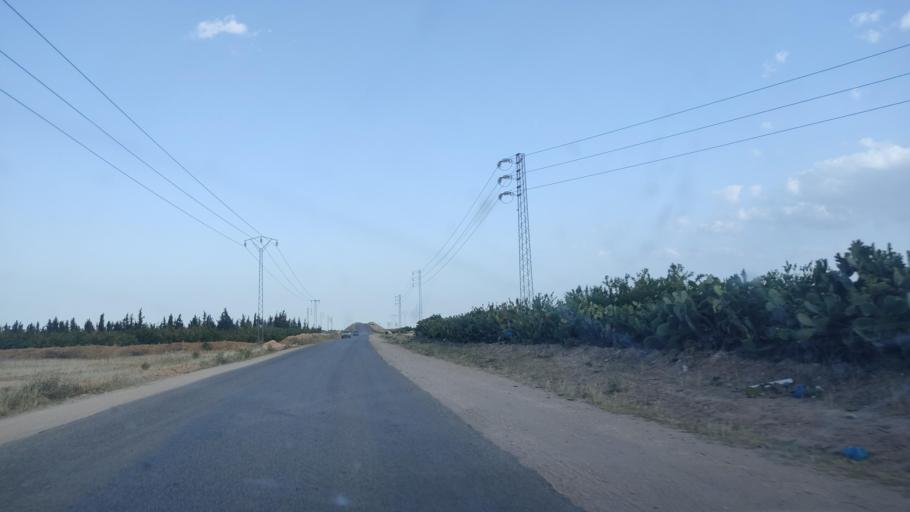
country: TN
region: Safaqis
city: Sfax
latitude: 34.8293
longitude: 10.6390
